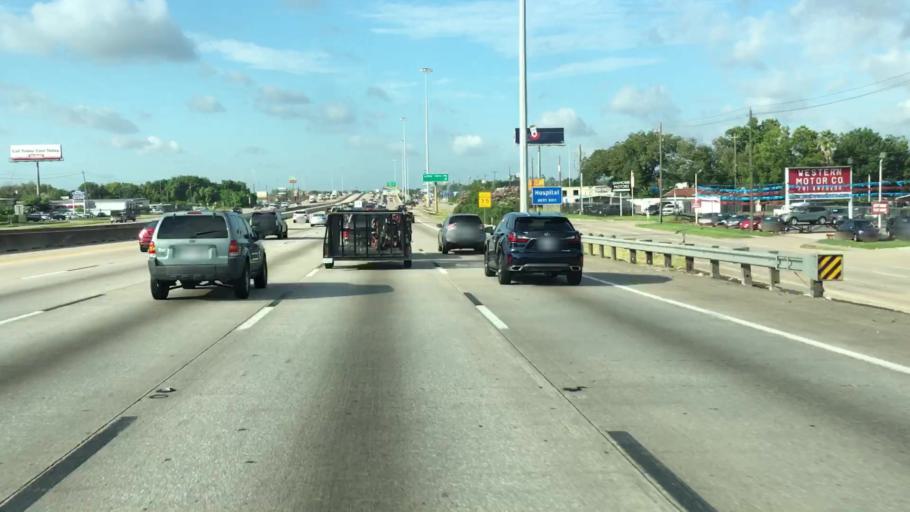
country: US
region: Texas
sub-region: Harris County
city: Aldine
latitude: 29.8773
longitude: -95.3262
